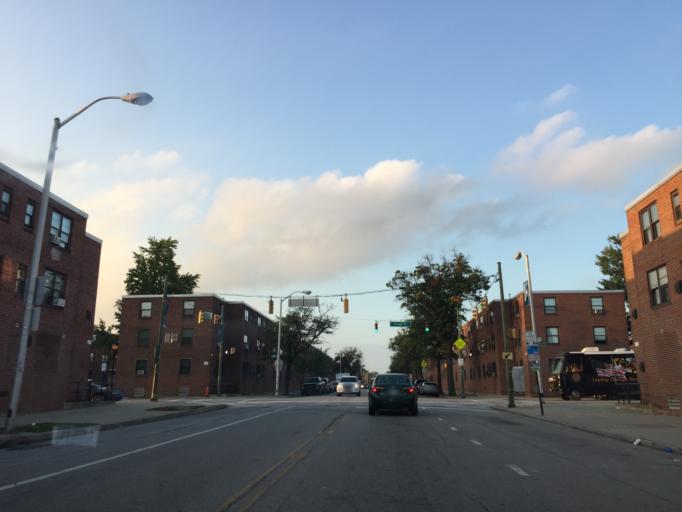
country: US
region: Maryland
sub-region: City of Baltimore
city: Baltimore
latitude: 39.2870
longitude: -76.5969
